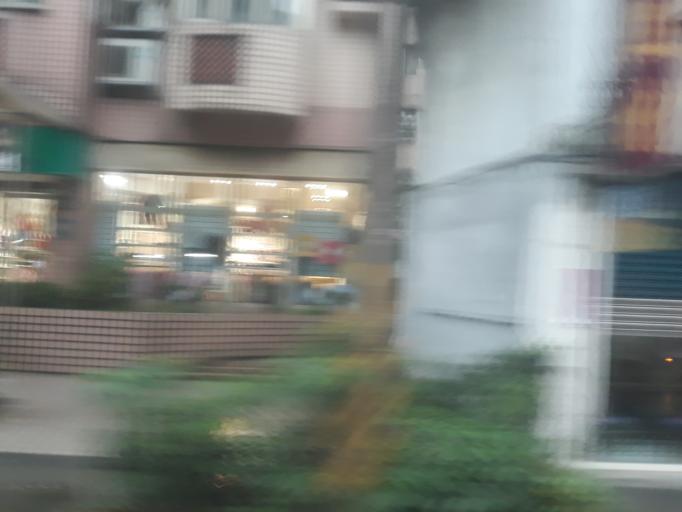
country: TW
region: Taipei
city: Taipei
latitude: 24.9883
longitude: 121.5651
